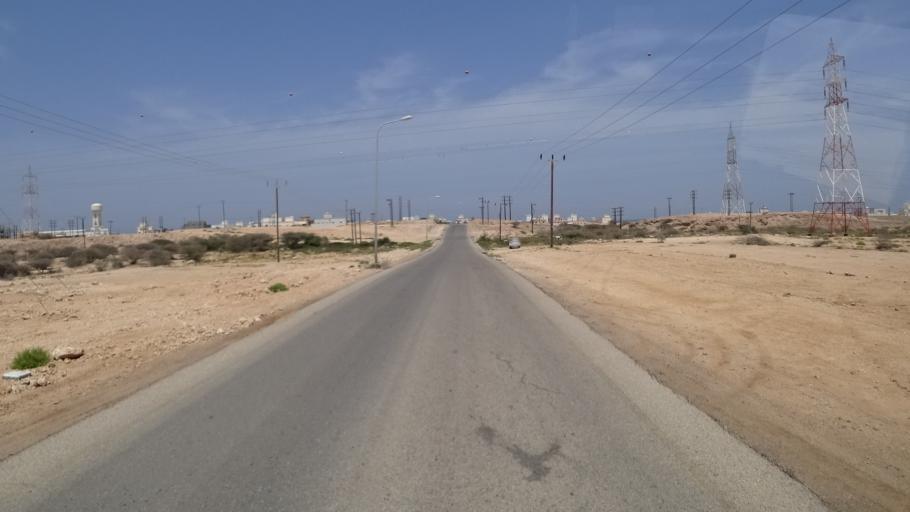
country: OM
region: Ash Sharqiyah
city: Sur
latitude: 22.6137
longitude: 59.4539
